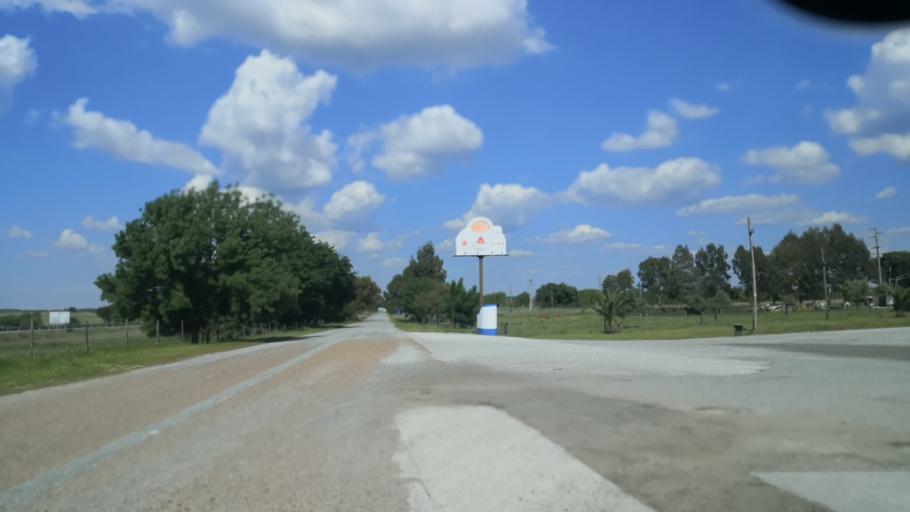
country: PT
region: Evora
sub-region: Arraiolos
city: Arraiolos
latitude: 38.7010
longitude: -8.0636
